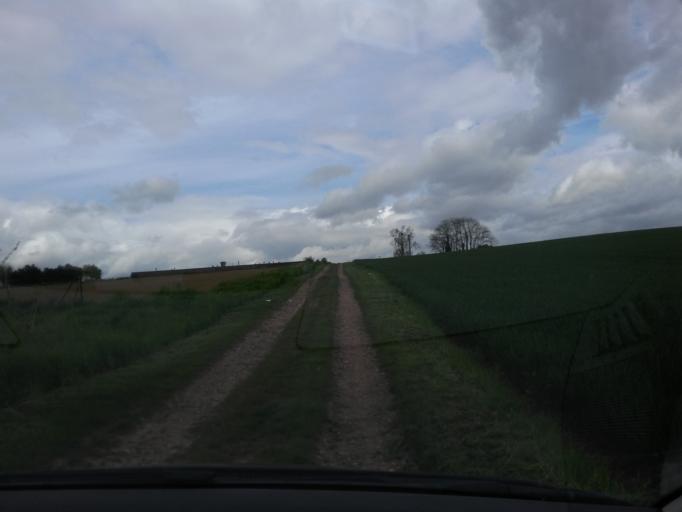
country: FR
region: Picardie
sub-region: Departement de l'Oise
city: Grandfresnoy
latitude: 49.3676
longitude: 2.6626
